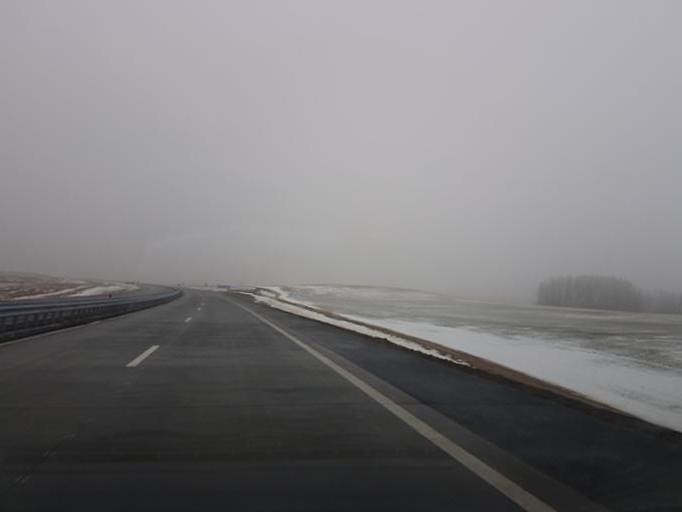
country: BY
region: Minsk
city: Atolina
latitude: 53.7555
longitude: 27.4091
